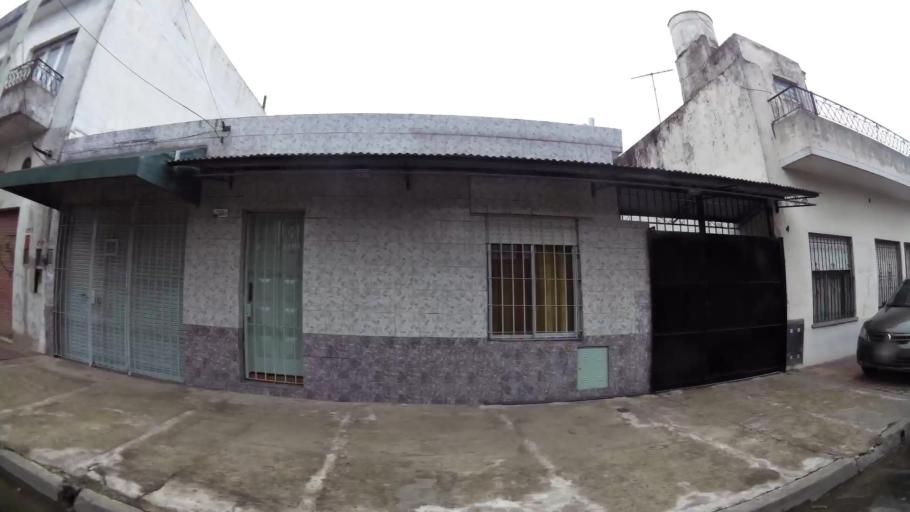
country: AR
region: Buenos Aires
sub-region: Partido de Lanus
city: Lanus
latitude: -34.7347
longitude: -58.3718
